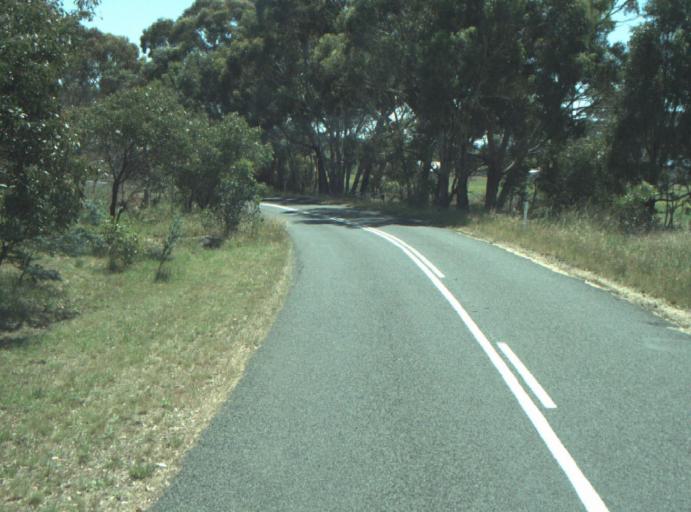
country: AU
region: Victoria
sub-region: Greater Geelong
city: Lara
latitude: -37.8565
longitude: 144.2809
